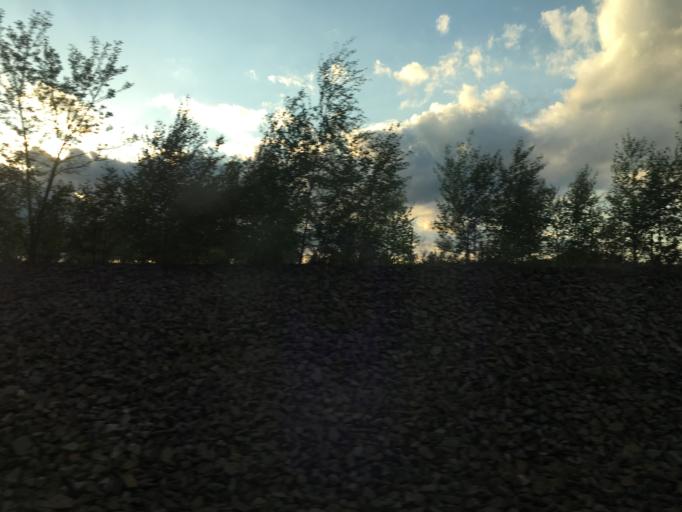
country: DE
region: Brandenburg
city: Hohenleipisch
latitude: 51.4883
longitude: 13.5581
